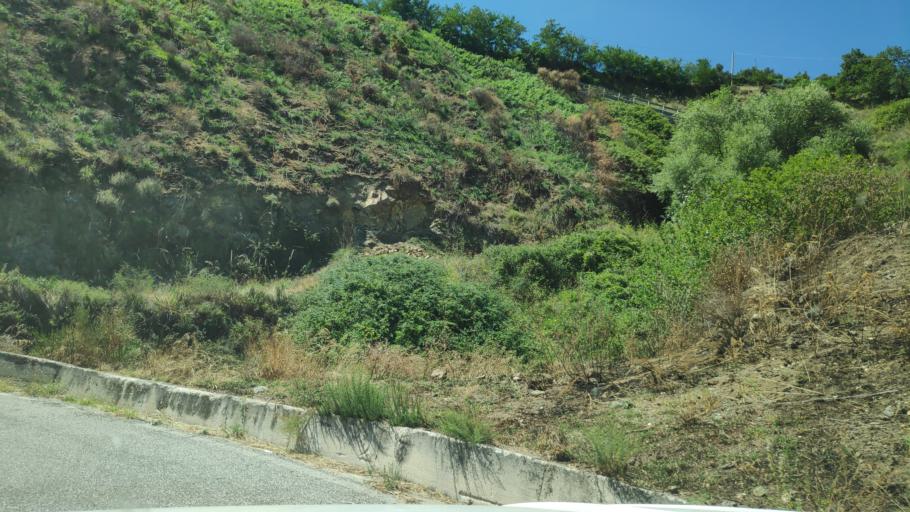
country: IT
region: Calabria
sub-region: Provincia di Catanzaro
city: Gasperina
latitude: 38.7446
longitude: 16.5085
